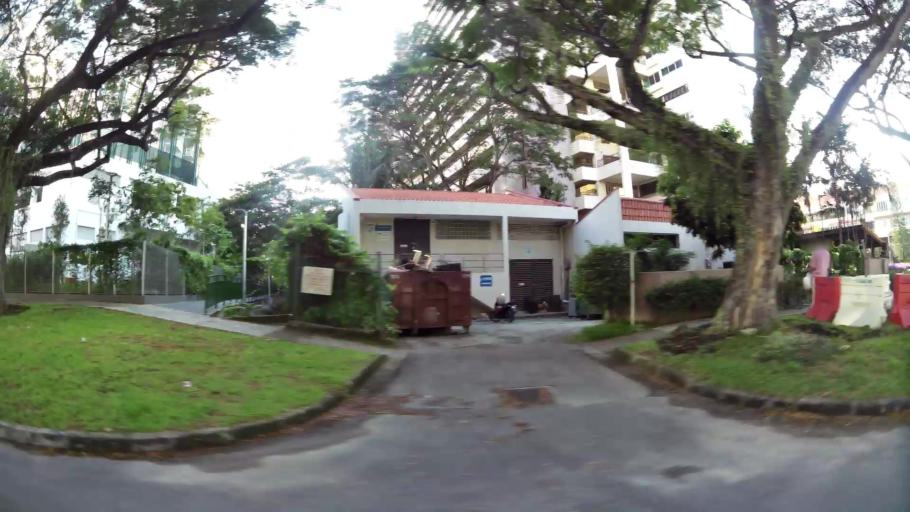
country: SG
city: Singapore
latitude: 1.3222
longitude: 103.9441
